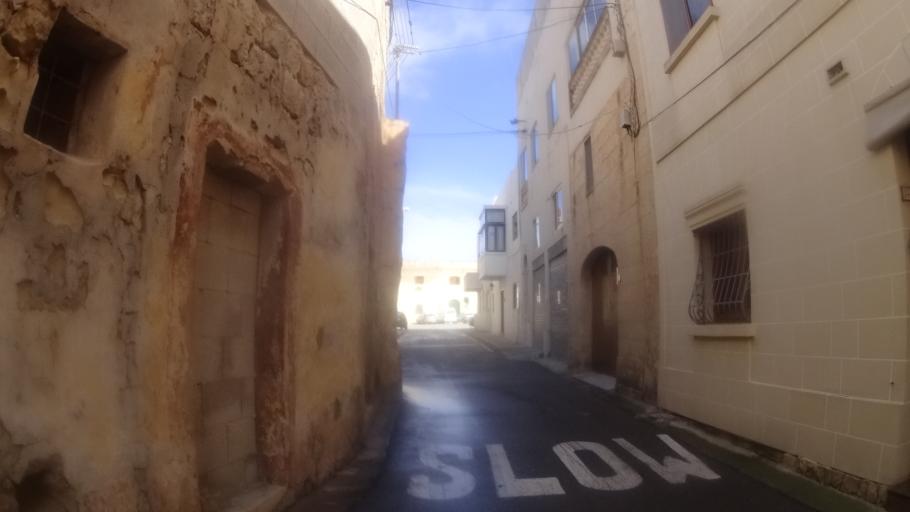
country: MT
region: In-Naxxar
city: Naxxar
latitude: 35.9156
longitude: 14.4449
